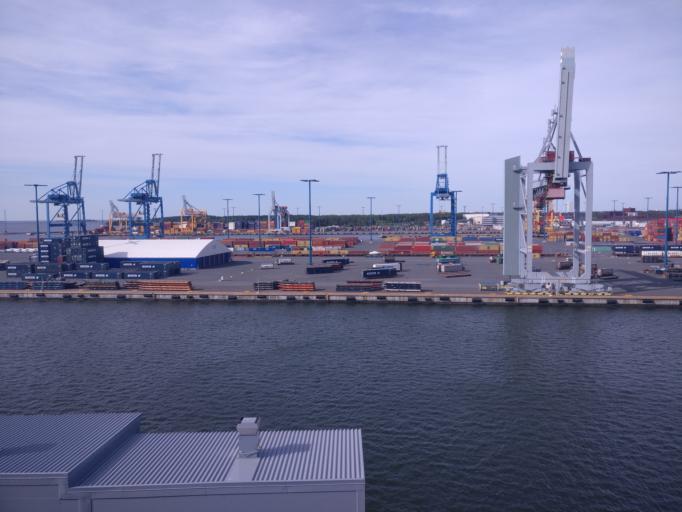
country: FI
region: Uusimaa
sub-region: Helsinki
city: Sibbo
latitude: 60.2195
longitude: 25.1992
